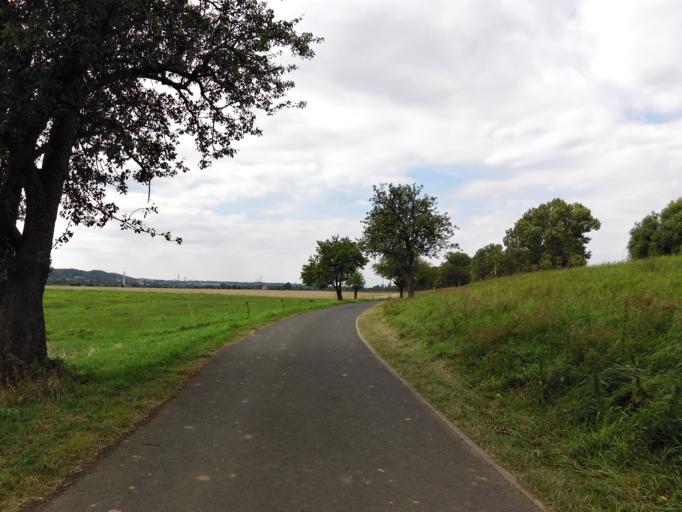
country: DE
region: Saxony
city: Radebeul
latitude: 51.0966
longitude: 13.6363
